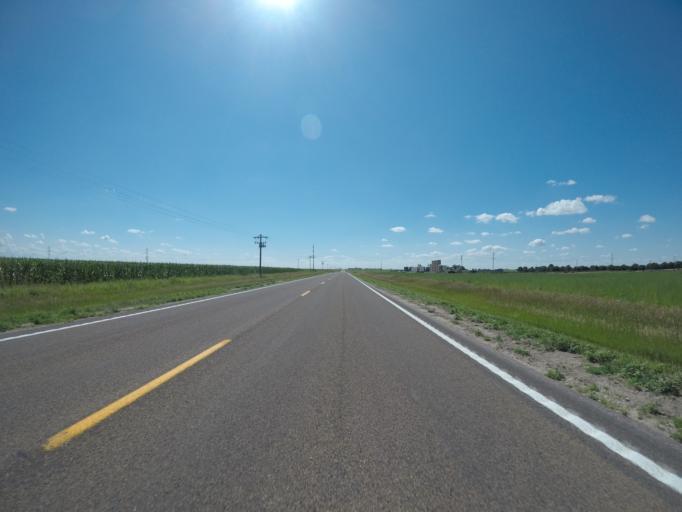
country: US
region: Nebraska
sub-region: Chase County
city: Imperial
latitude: 40.5376
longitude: -101.7398
